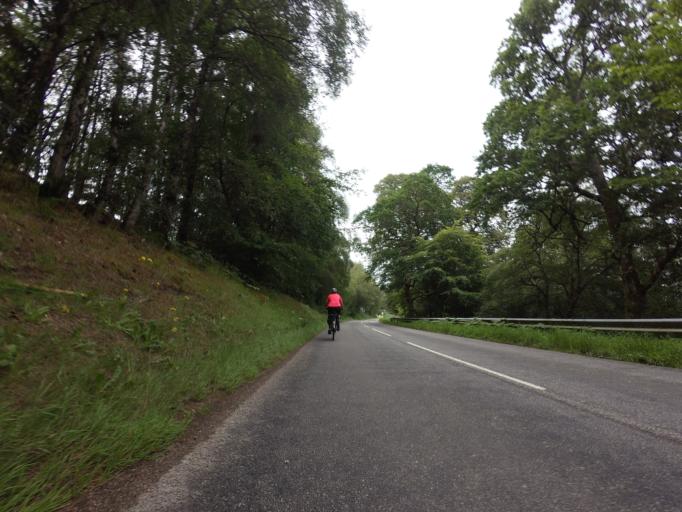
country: GB
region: Scotland
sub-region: Highland
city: Alness
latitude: 57.8524
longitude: -4.3002
